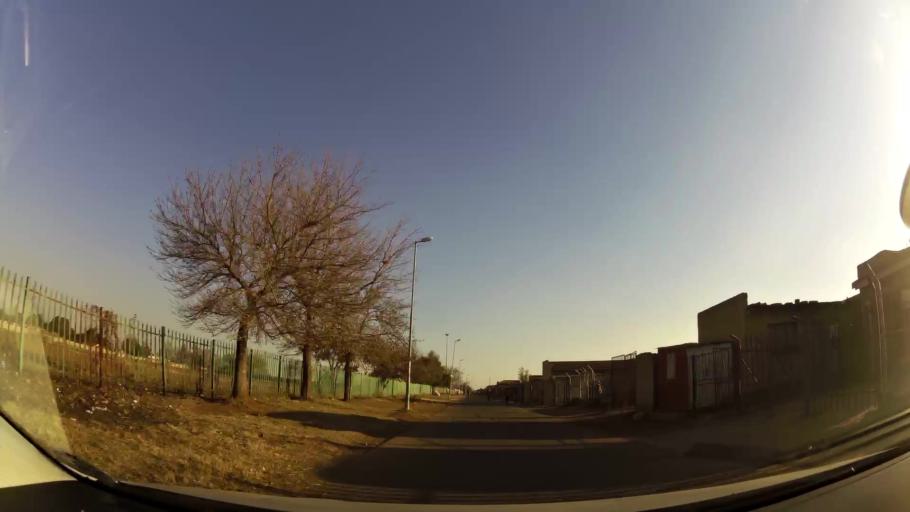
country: ZA
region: Gauteng
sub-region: City of Johannesburg Metropolitan Municipality
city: Soweto
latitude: -26.2530
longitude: 27.8834
